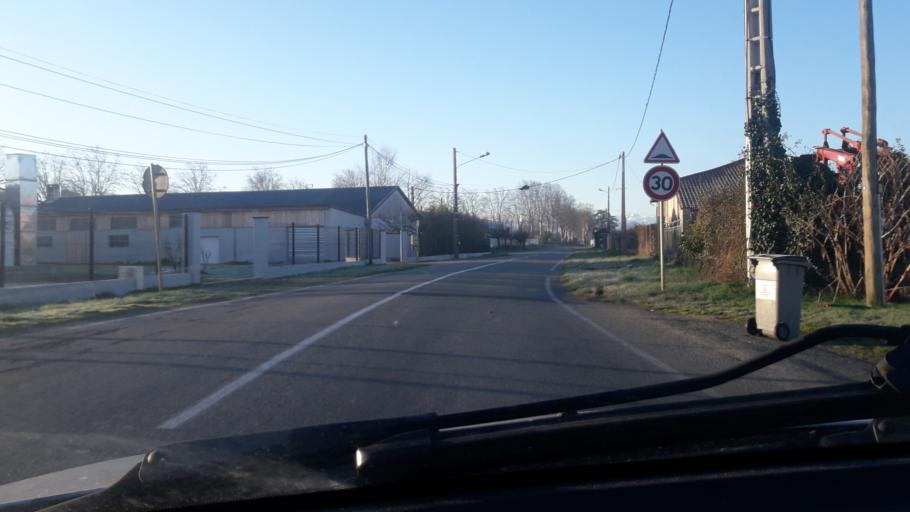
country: FR
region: Midi-Pyrenees
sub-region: Departement de la Haute-Garonne
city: Carbonne
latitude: 43.3089
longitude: 1.2229
